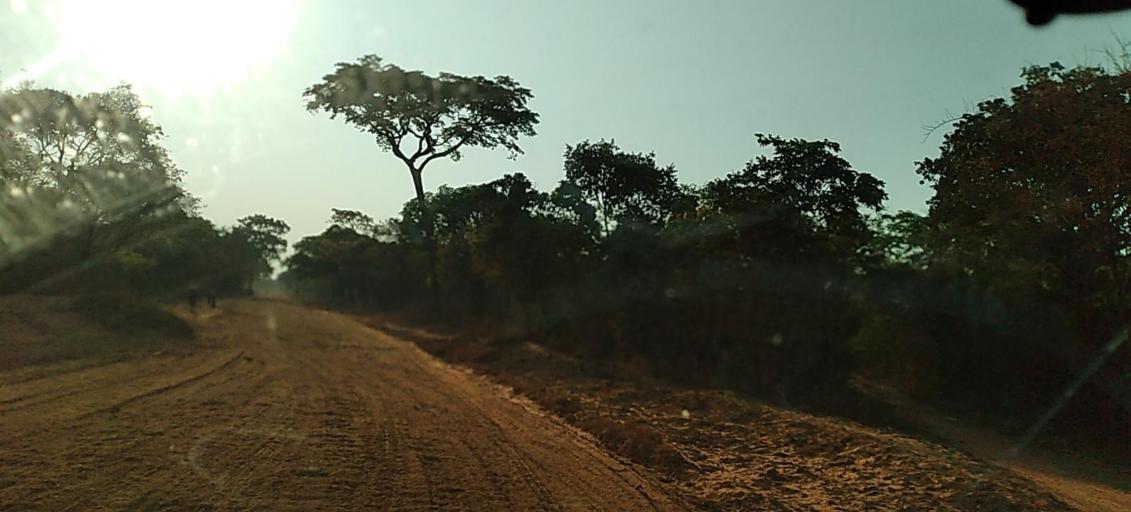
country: ZM
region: North-Western
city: Kasempa
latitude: -13.4718
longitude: 25.8662
